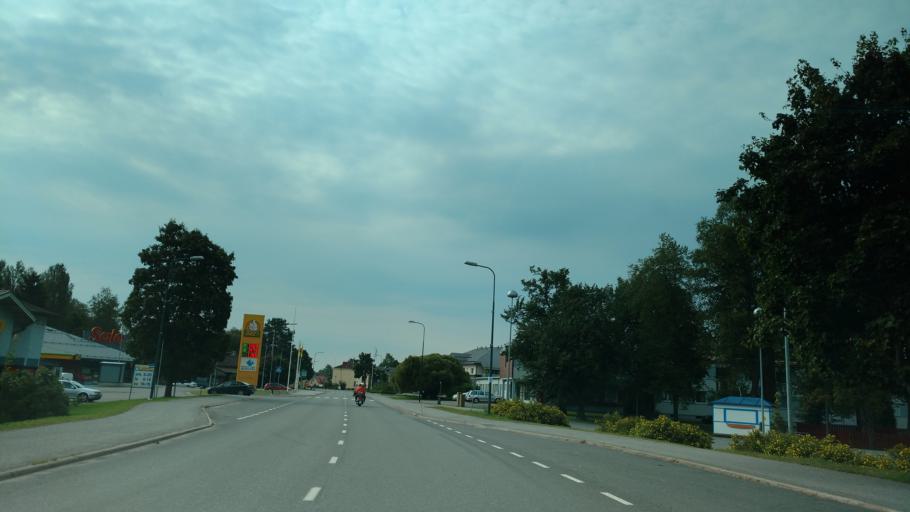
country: FI
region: Varsinais-Suomi
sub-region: Loimaa
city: Koski Tl
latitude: 60.6565
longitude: 23.1413
